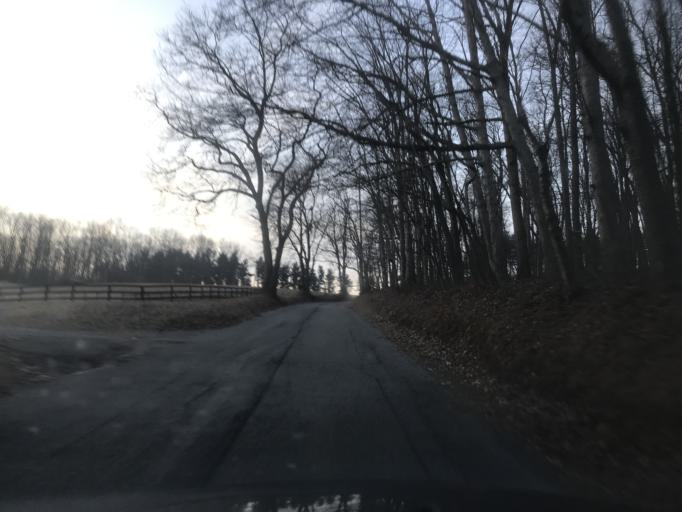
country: US
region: Pennsylvania
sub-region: York County
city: New Freedom
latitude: 39.6774
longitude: -76.7060
